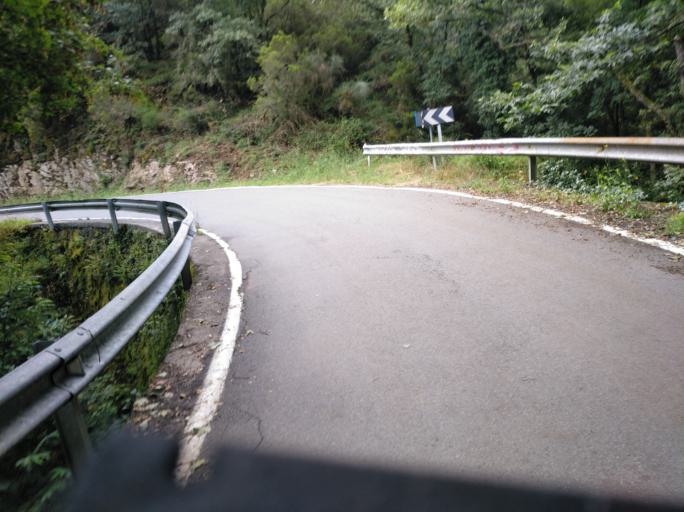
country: ES
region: Galicia
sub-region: Provincia de Ourense
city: Castro Caldelas
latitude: 42.3841
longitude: -7.4621
